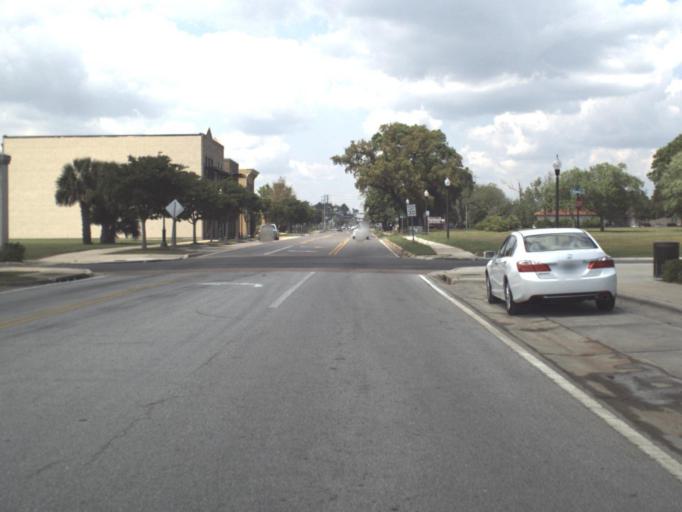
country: US
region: Florida
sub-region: Escambia County
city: Pensacola
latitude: 30.4128
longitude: -87.2047
